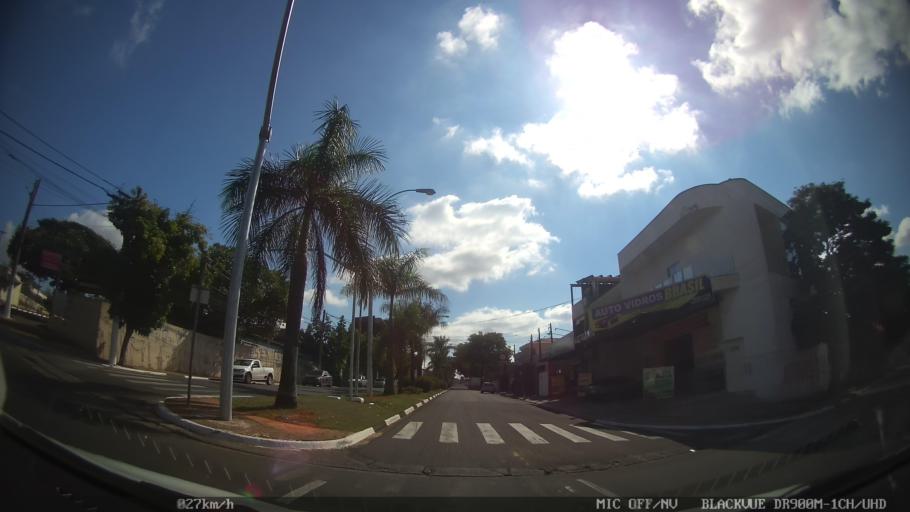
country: BR
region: Sao Paulo
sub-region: Hortolandia
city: Hortolandia
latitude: -22.8527
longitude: -47.2160
